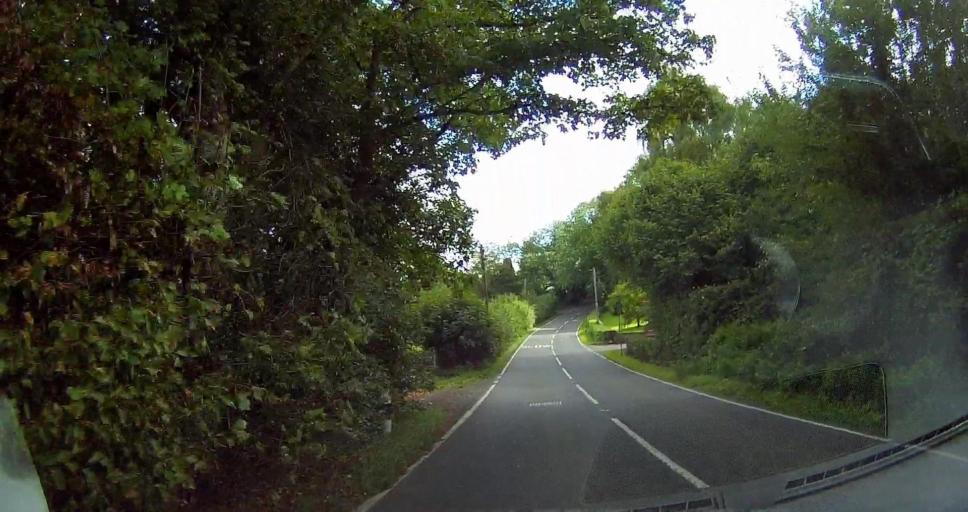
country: GB
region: England
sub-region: Cheshire East
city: Chorlton
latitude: 52.9805
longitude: -2.4122
